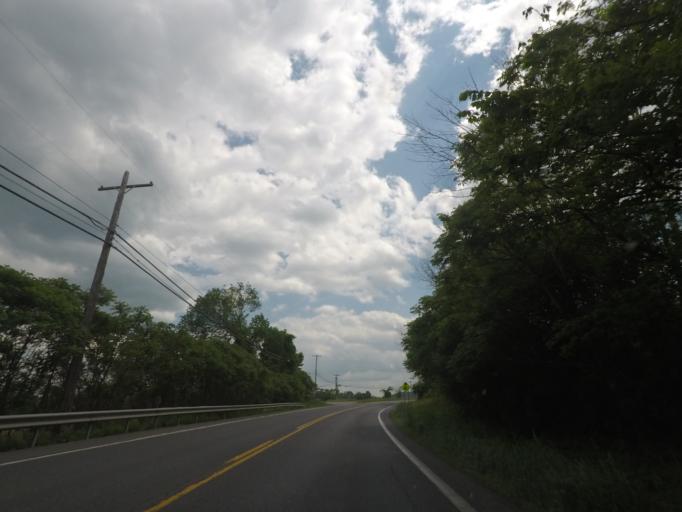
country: US
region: New York
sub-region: Dutchess County
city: Dover Plains
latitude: 41.8828
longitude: -73.5284
